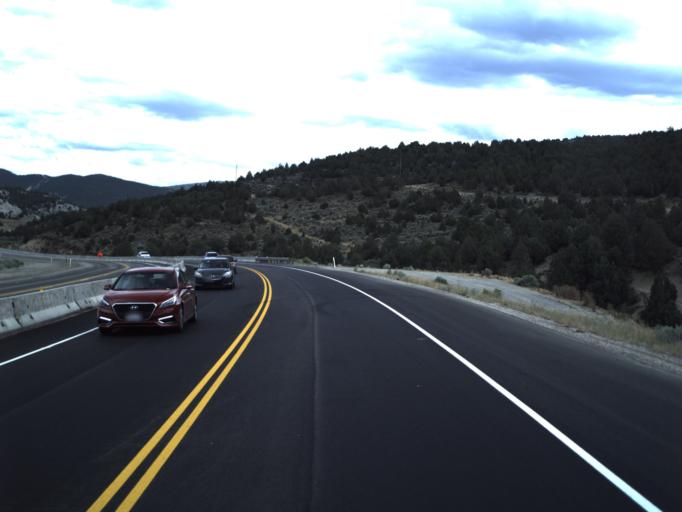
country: US
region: Utah
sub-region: Utah County
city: Mapleton
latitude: 39.9554
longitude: -111.2401
